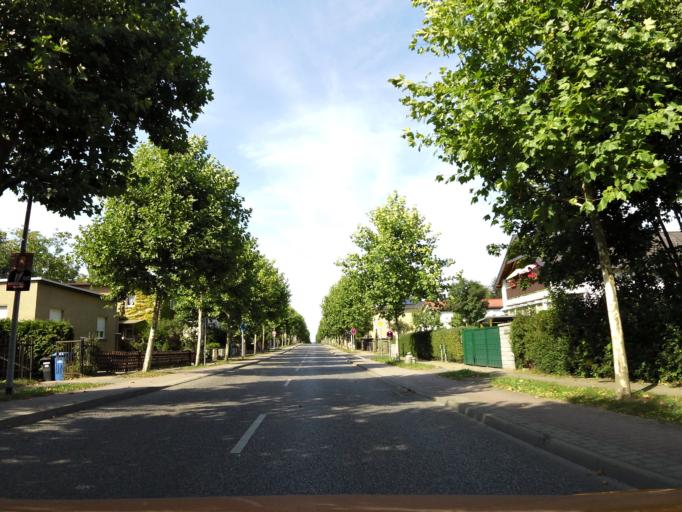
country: DE
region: Brandenburg
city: Teltow
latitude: 52.3842
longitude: 13.2473
